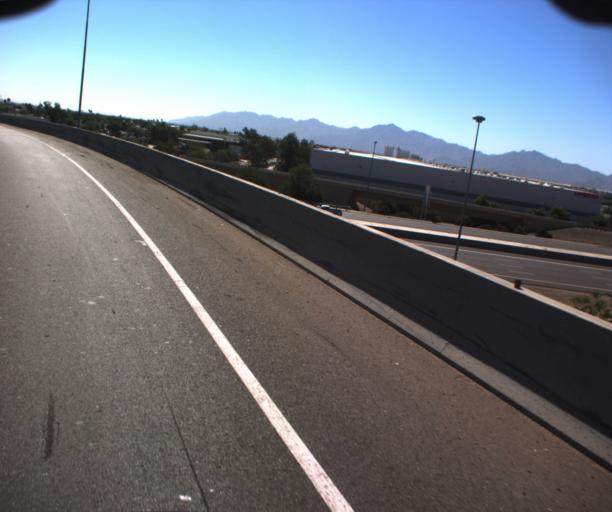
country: US
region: Arizona
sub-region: Maricopa County
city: Tolleson
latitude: 33.4625
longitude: -112.2686
